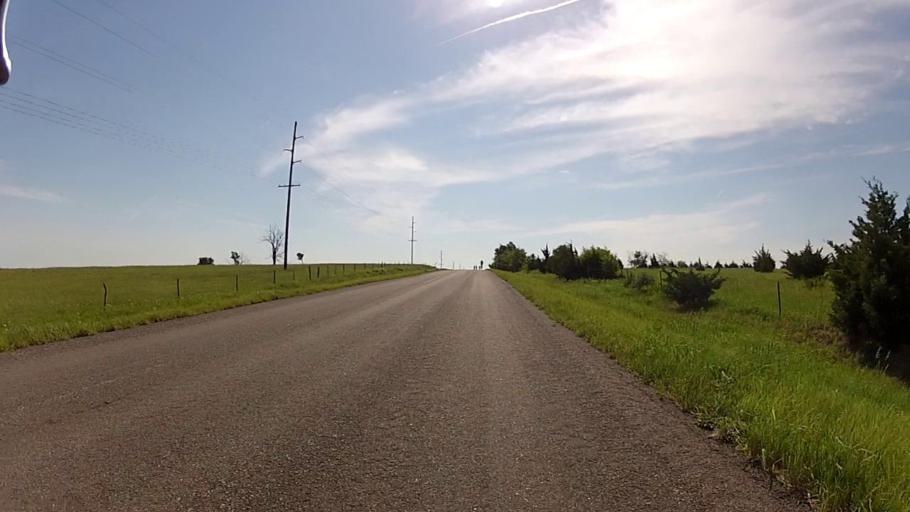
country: US
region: Kansas
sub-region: Cowley County
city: Winfield
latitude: 37.0711
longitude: -96.6489
